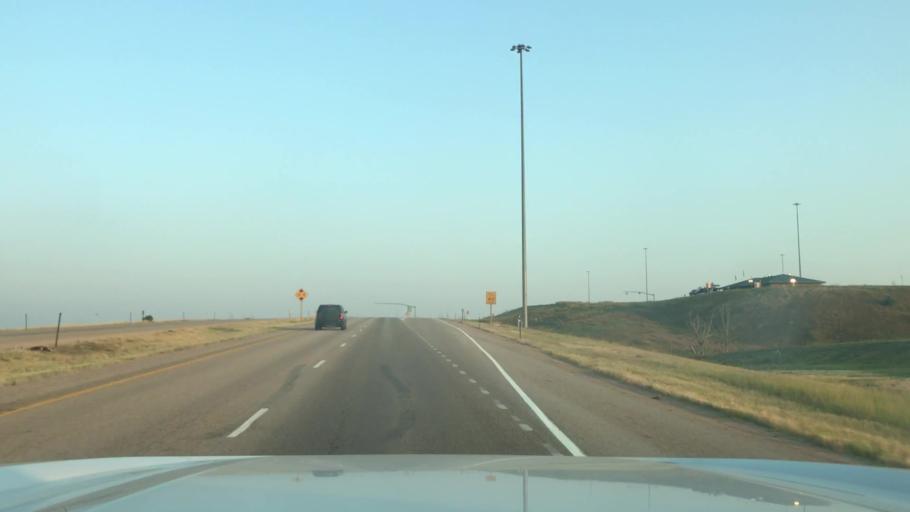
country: US
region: Wyoming
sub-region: Sheridan County
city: Sheridan
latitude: 44.8902
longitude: -107.0097
